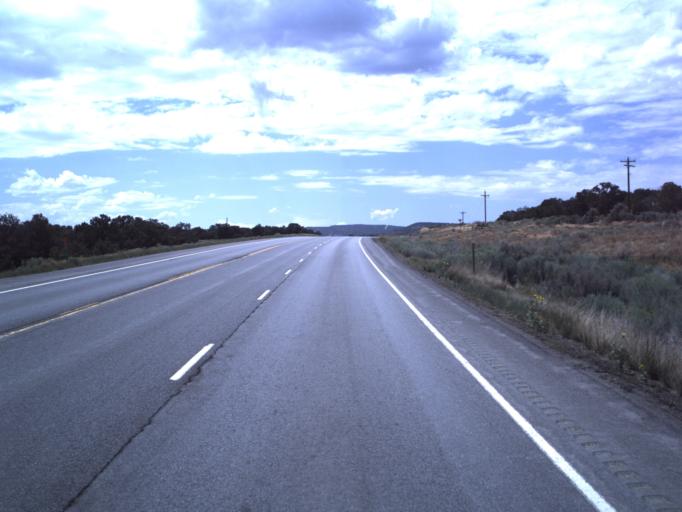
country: US
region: Utah
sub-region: Duchesne County
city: Duchesne
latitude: 40.1714
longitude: -110.5646
